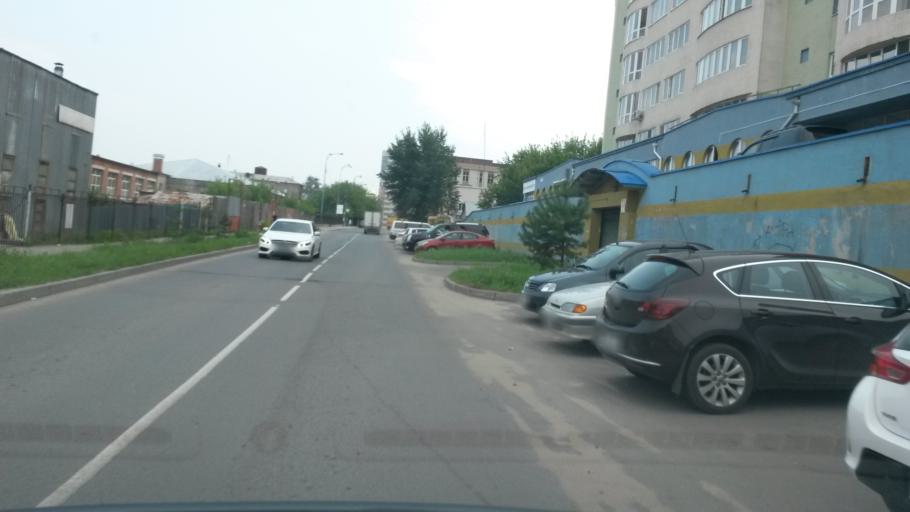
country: RU
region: Ivanovo
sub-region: Gorod Ivanovo
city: Ivanovo
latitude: 57.0025
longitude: 40.9663
